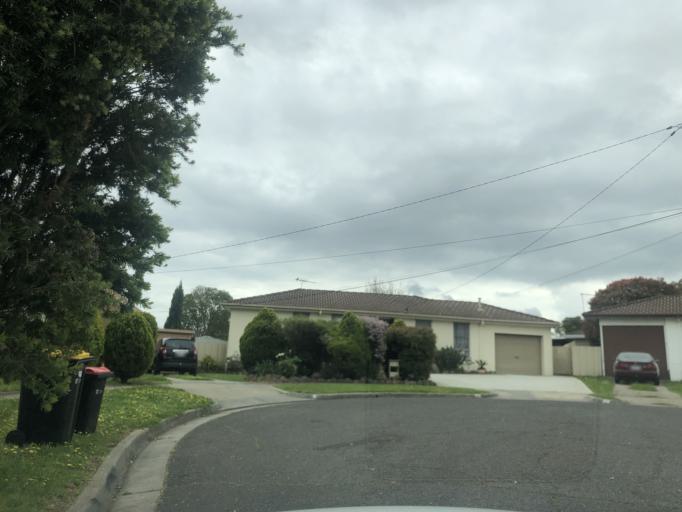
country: AU
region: Victoria
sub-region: Greater Dandenong
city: Noble Park North
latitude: -37.9570
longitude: 145.1959
